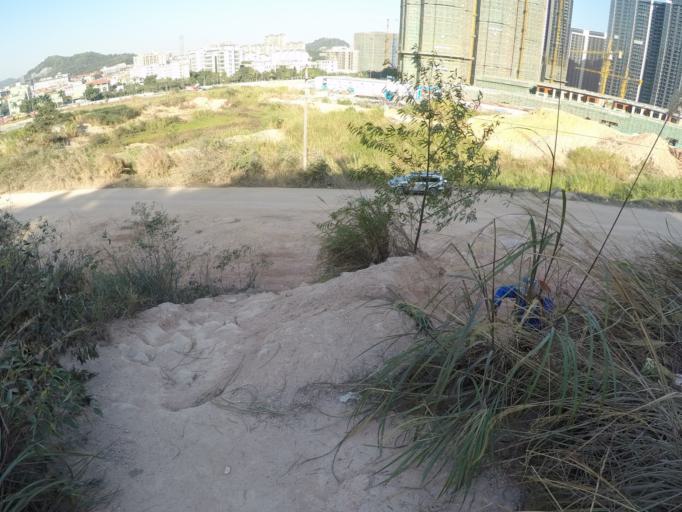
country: CN
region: Guangdong
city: Dongqu
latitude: 22.4834
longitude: 113.4138
